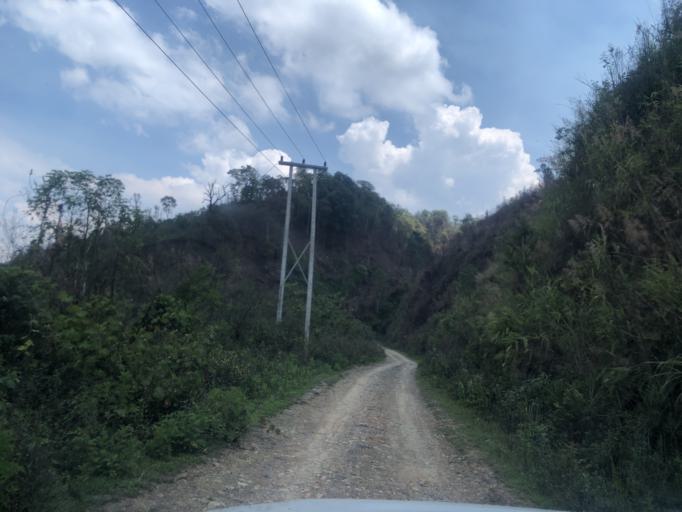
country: LA
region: Phongsali
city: Phongsali
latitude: 21.3994
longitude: 102.1897
